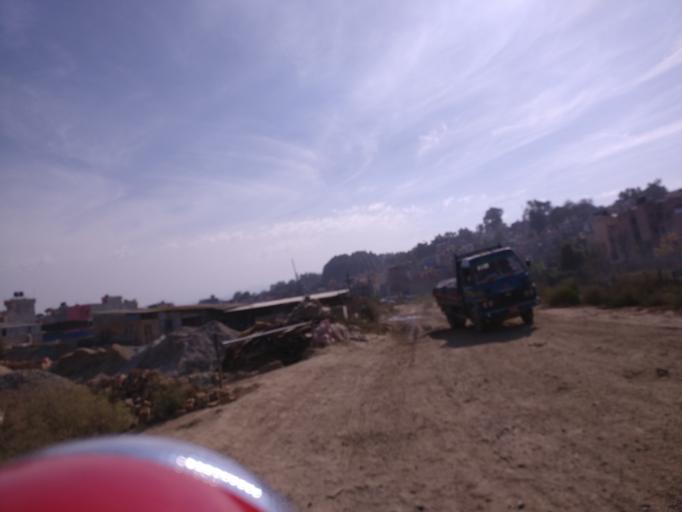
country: NP
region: Central Region
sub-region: Bagmati Zone
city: Patan
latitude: 27.6611
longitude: 85.3079
